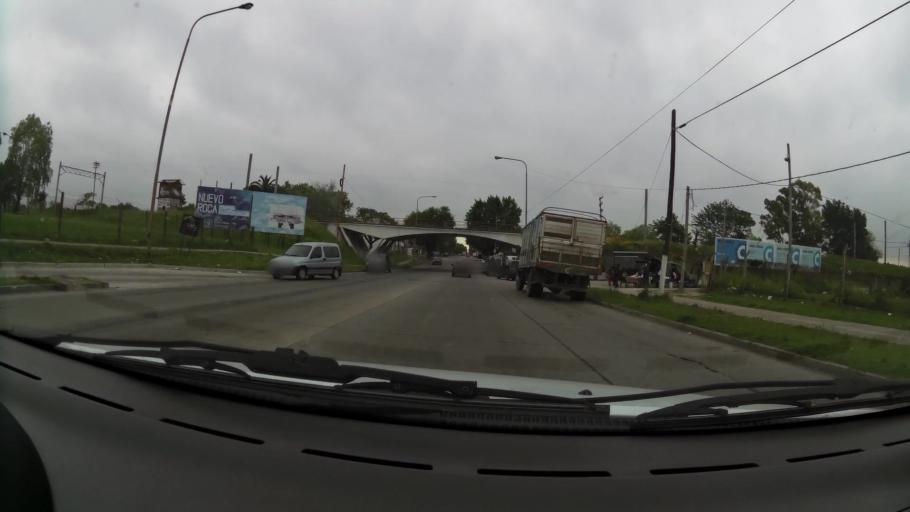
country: AR
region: Buenos Aires
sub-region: Partido de La Plata
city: La Plata
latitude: -34.8843
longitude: -57.9759
